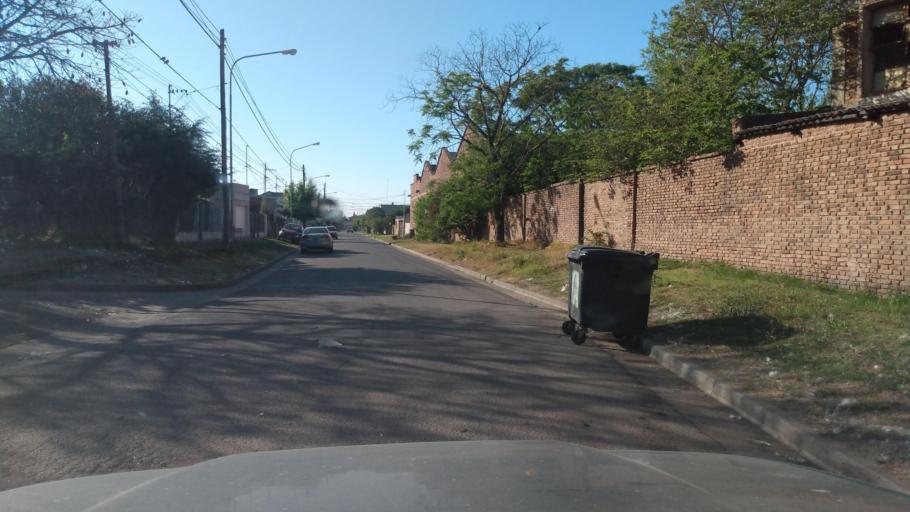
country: AR
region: Buenos Aires
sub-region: Partido de Lujan
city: Lujan
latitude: -34.5565
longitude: -59.1132
